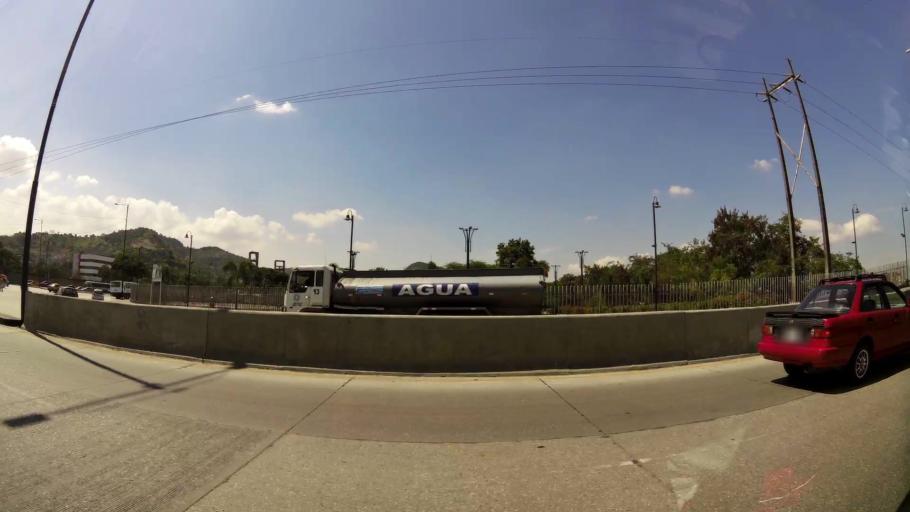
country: EC
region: Guayas
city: Guayaquil
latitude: -2.1953
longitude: -79.9372
